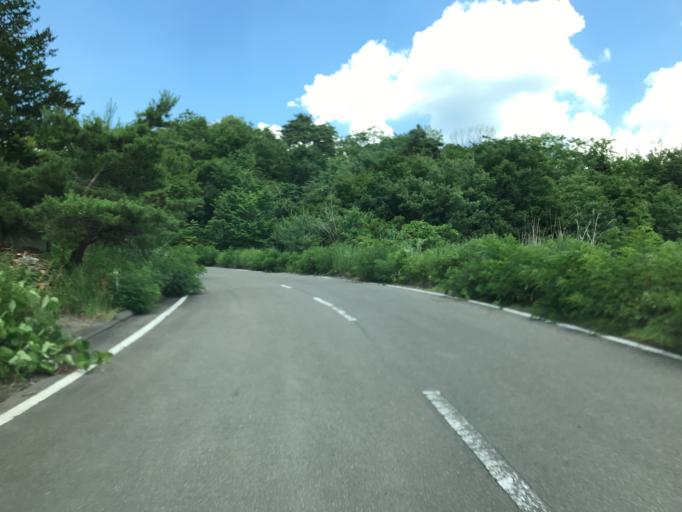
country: JP
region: Fukushima
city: Yanagawamachi-saiwaicho
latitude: 37.7591
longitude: 140.6857
